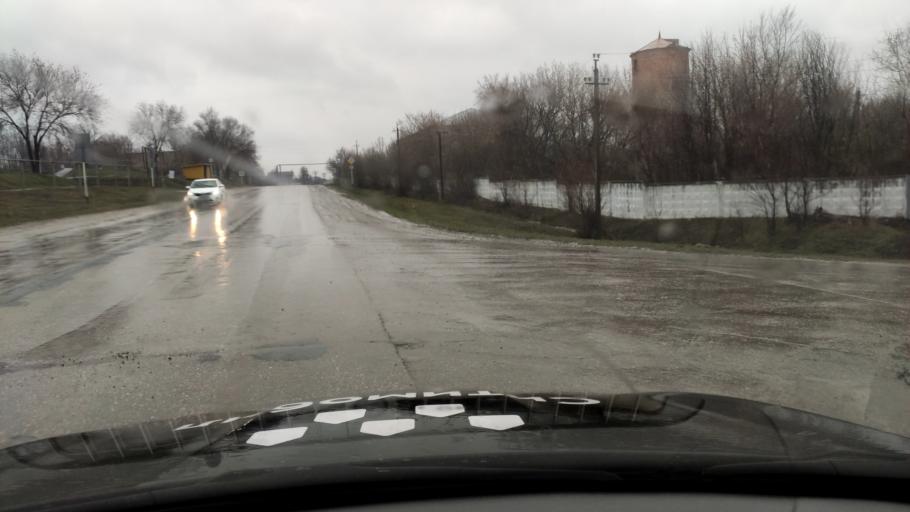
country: RU
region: Samara
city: Balasheyka
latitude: 53.2305
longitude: 48.2367
